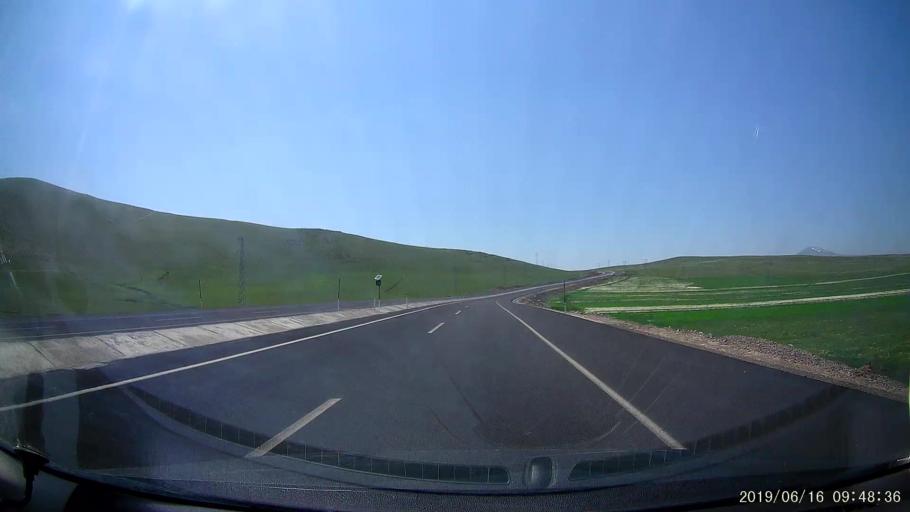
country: TR
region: Kars
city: Digor
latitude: 40.4318
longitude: 43.3543
